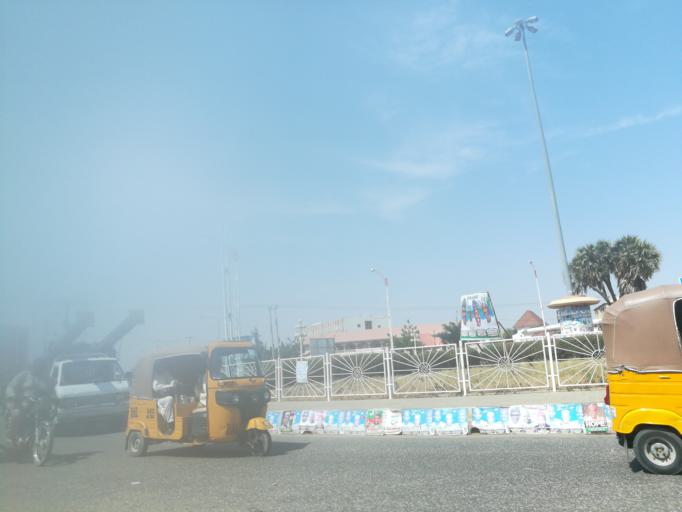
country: NG
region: Kano
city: Kano
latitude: 12.0276
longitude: 8.5154
